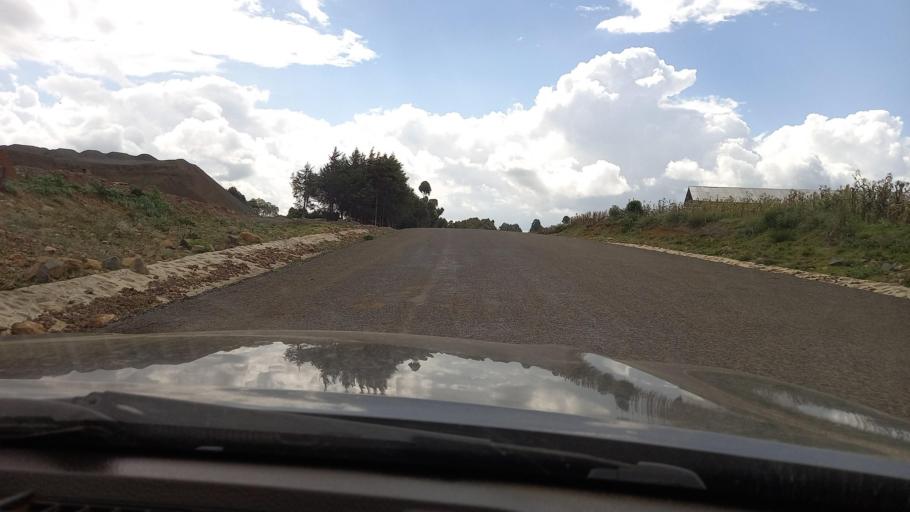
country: ET
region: Southern Nations, Nationalities, and People's Region
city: Mizan Teferi
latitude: 6.2144
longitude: 35.6264
